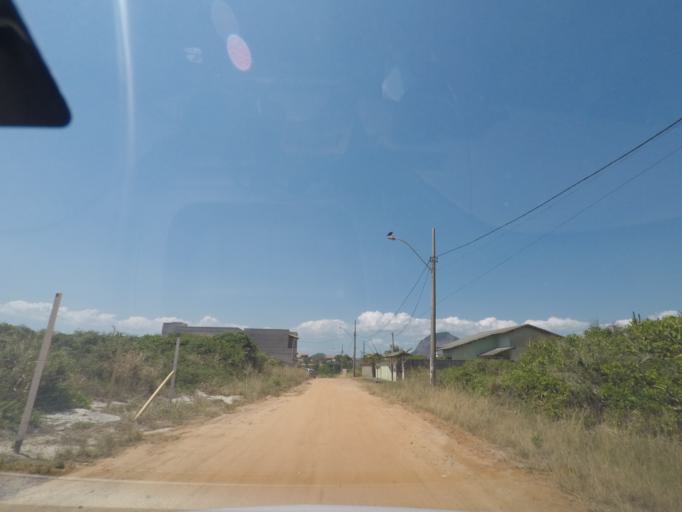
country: BR
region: Rio de Janeiro
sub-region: Marica
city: Marica
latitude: -22.9733
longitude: -42.9298
